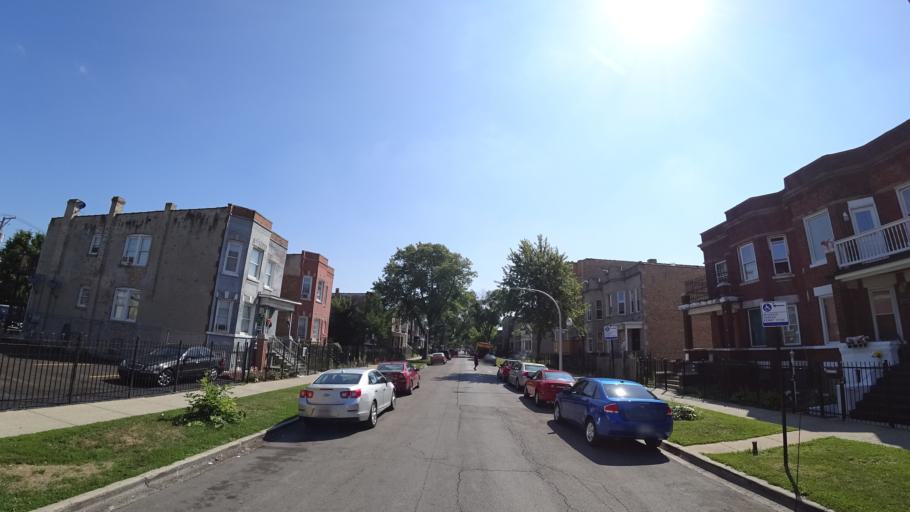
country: US
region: Illinois
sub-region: Cook County
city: Cicero
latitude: 41.8727
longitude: -87.7130
